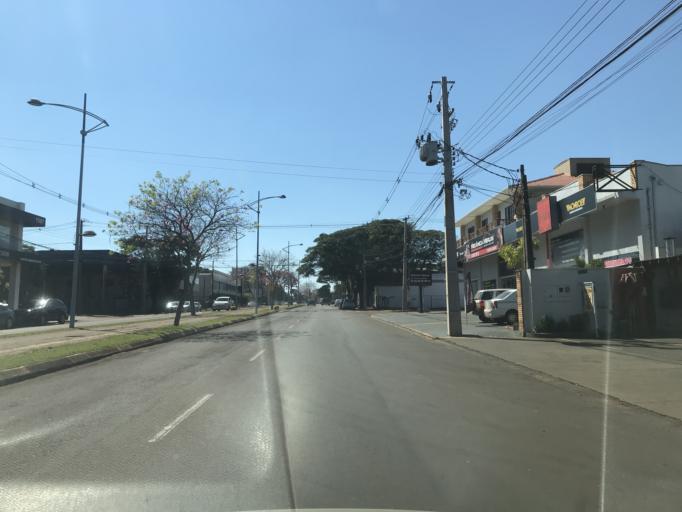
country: BR
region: Parana
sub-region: Toledo
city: Toledo
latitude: -24.7248
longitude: -53.7235
